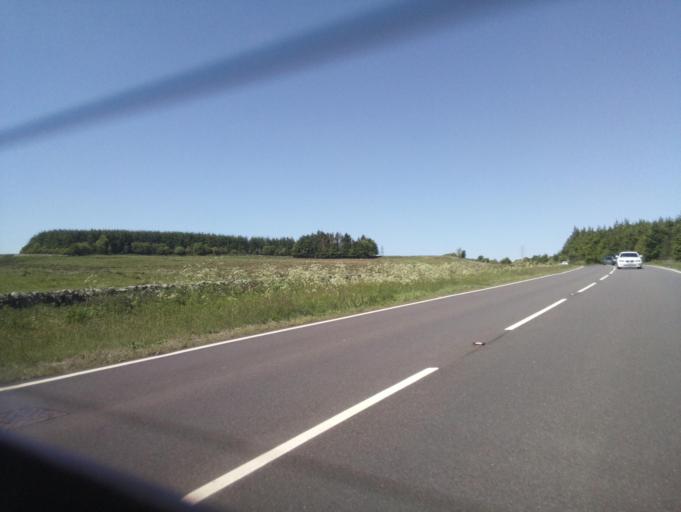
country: GB
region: Scotland
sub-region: The Scottish Borders
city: Hawick
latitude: 55.4702
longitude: -2.7928
